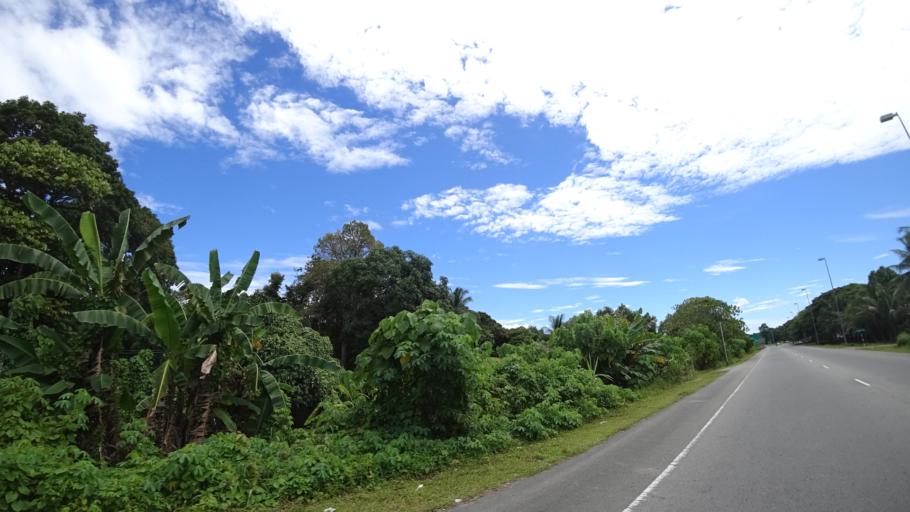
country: BN
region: Tutong
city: Tutong
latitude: 4.7687
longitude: 114.8204
